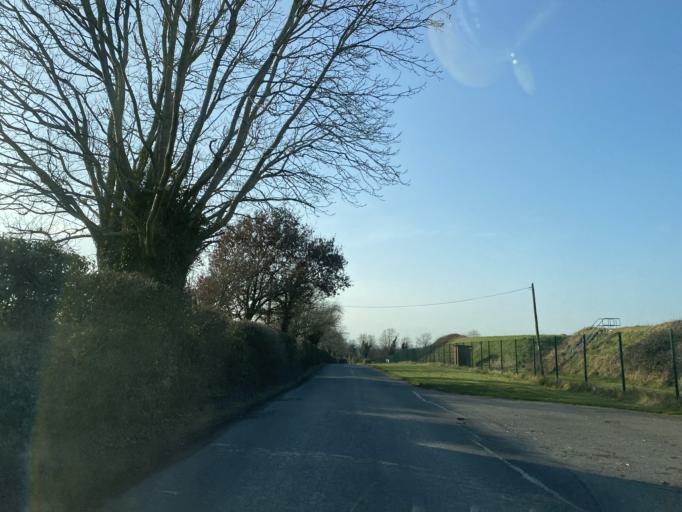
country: IE
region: Leinster
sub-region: Kildare
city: Maynooth
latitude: 53.3632
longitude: -6.5695
